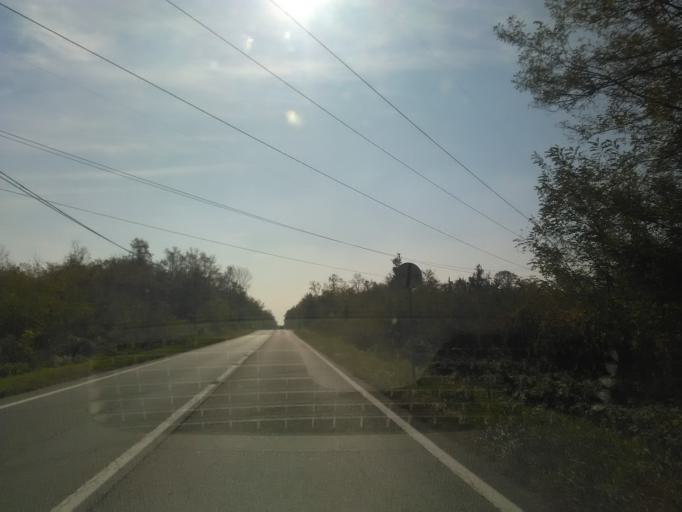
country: IT
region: Piedmont
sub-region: Provincia di Vercelli
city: Gattinara
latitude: 45.5875
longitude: 8.3729
